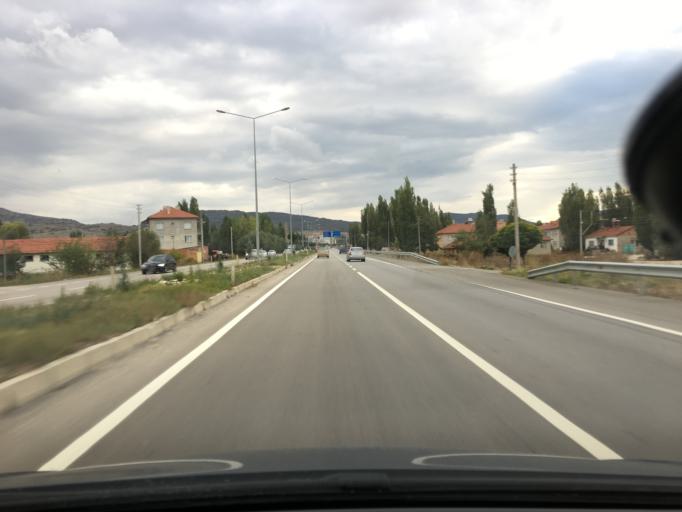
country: TR
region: Afyonkarahisar
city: Sincanli
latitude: 38.7349
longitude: 30.3485
